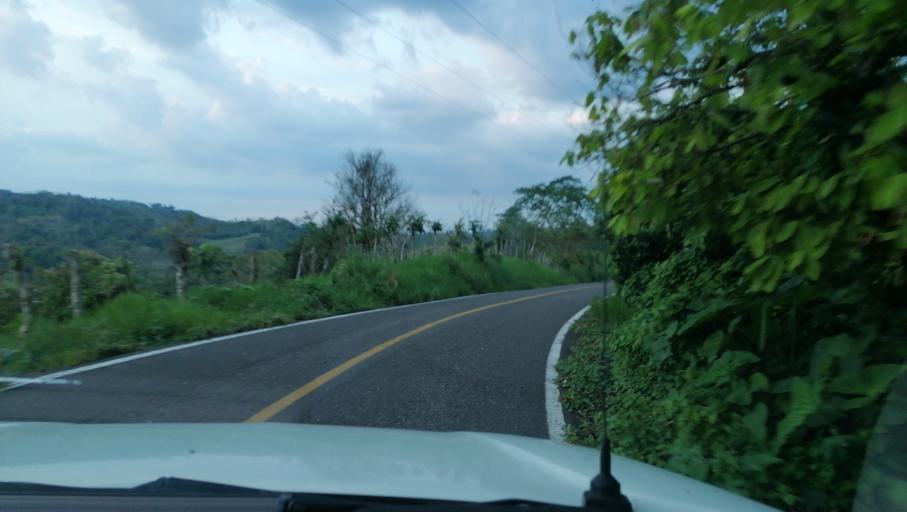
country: MX
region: Chiapas
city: Pichucalco
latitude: 17.5289
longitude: -93.1542
